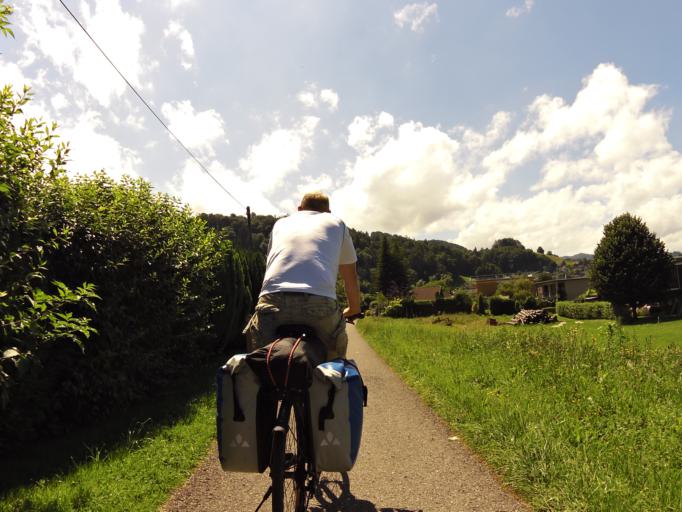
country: AT
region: Vorarlberg
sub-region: Politischer Bezirk Bregenz
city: Gaissau
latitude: 47.4634
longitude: 9.6027
